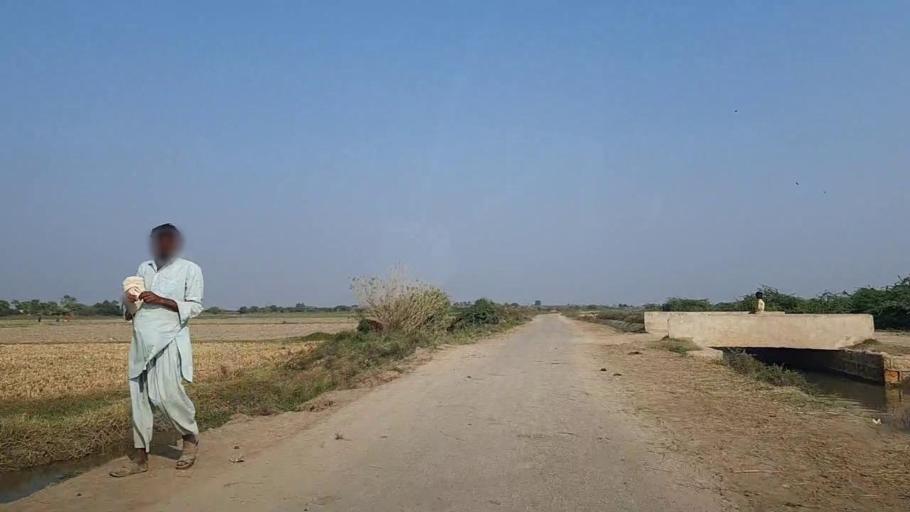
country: PK
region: Sindh
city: Mirpur Sakro
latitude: 24.6151
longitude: 67.7061
